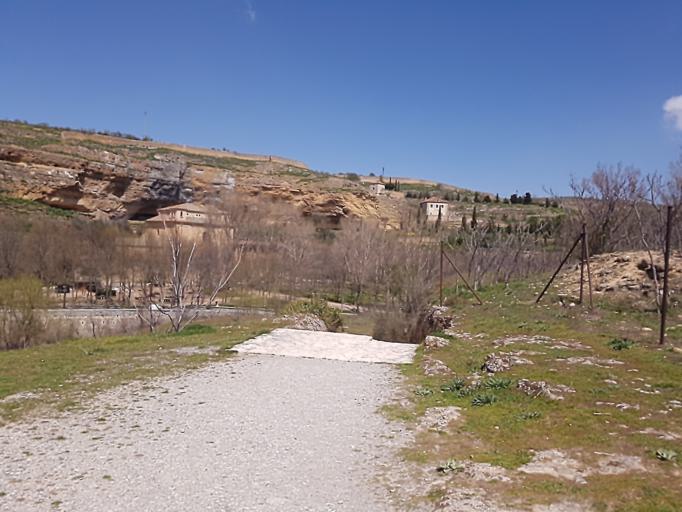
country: ES
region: Castille and Leon
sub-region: Provincia de Segovia
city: Segovia
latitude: 40.9549
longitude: -4.1358
